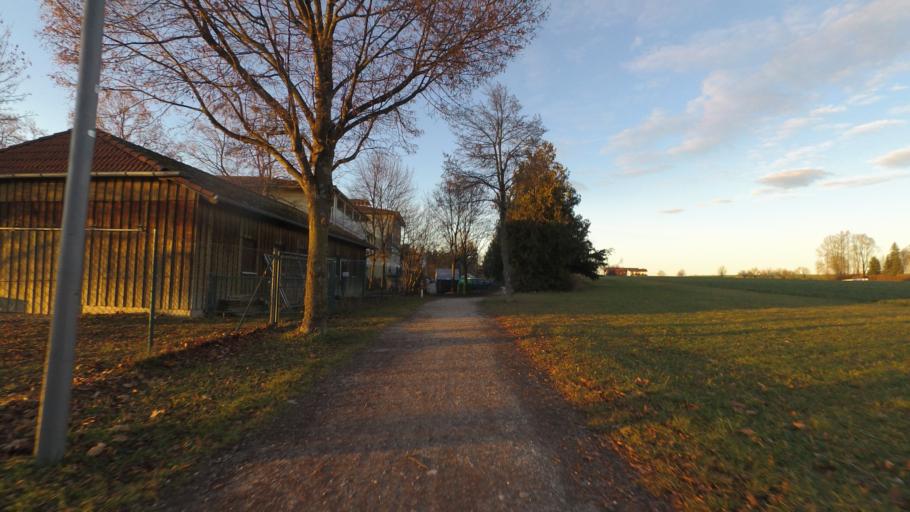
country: DE
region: Bavaria
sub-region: Upper Bavaria
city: Chieming
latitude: 47.8938
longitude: 12.5309
